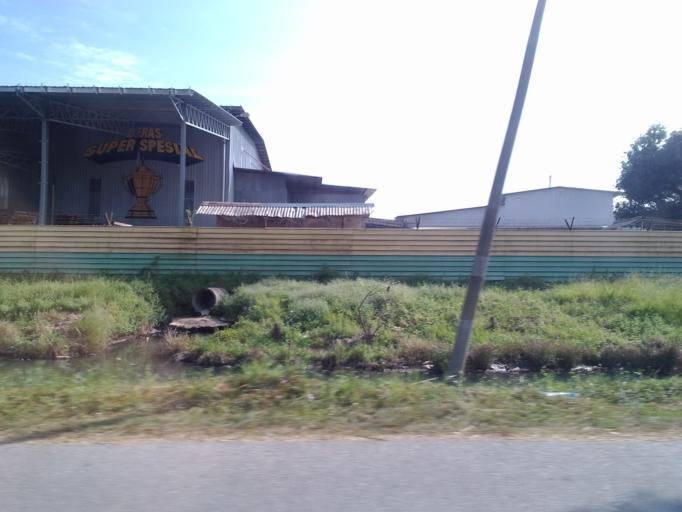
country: MY
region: Kedah
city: Gurun
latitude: 5.9591
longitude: 100.4056
